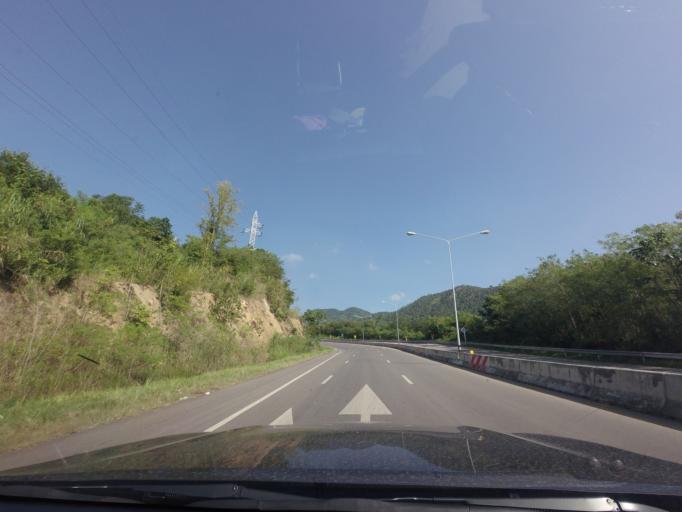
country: TH
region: Phetchabun
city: Lom Sak
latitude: 16.7654
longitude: 101.1404
